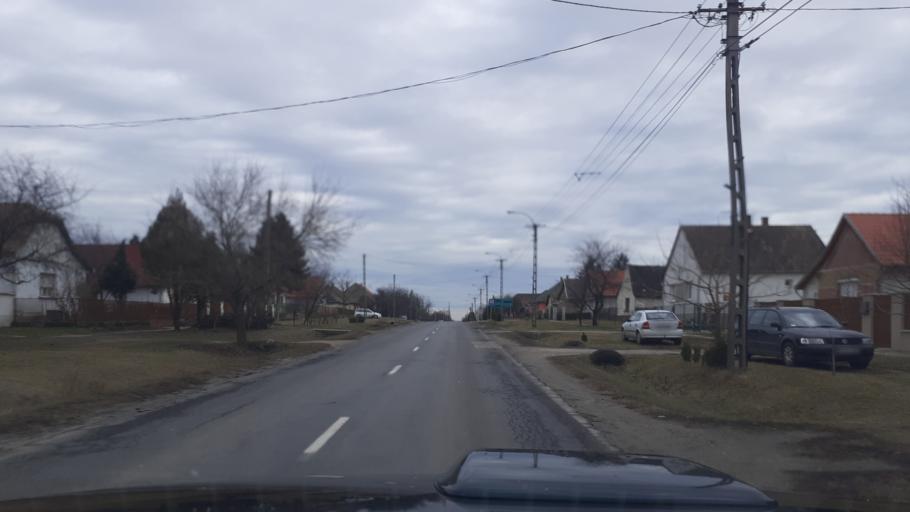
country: HU
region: Fejer
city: Mezofalva
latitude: 46.9311
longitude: 18.7836
